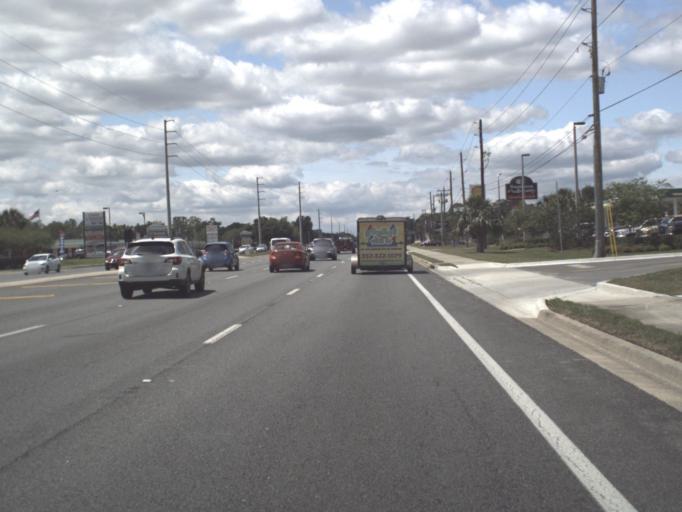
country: US
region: Florida
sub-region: Marion County
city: Ocala
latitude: 29.1167
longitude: -82.2193
